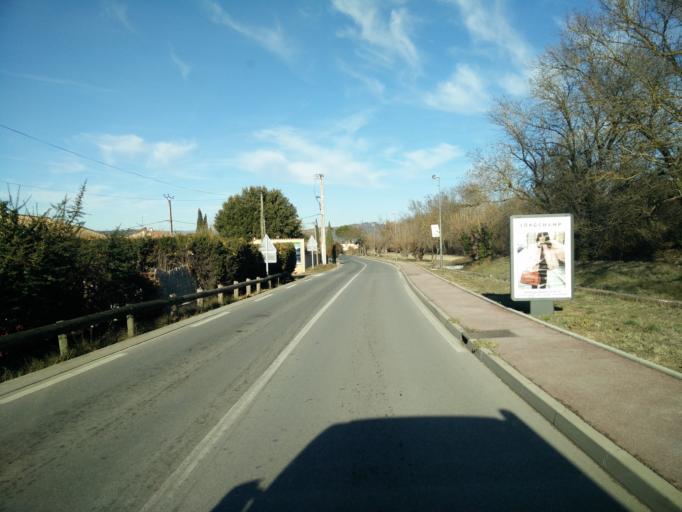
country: FR
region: Provence-Alpes-Cote d'Azur
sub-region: Departement du Var
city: Vidauban
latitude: 43.4161
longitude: 6.4274
